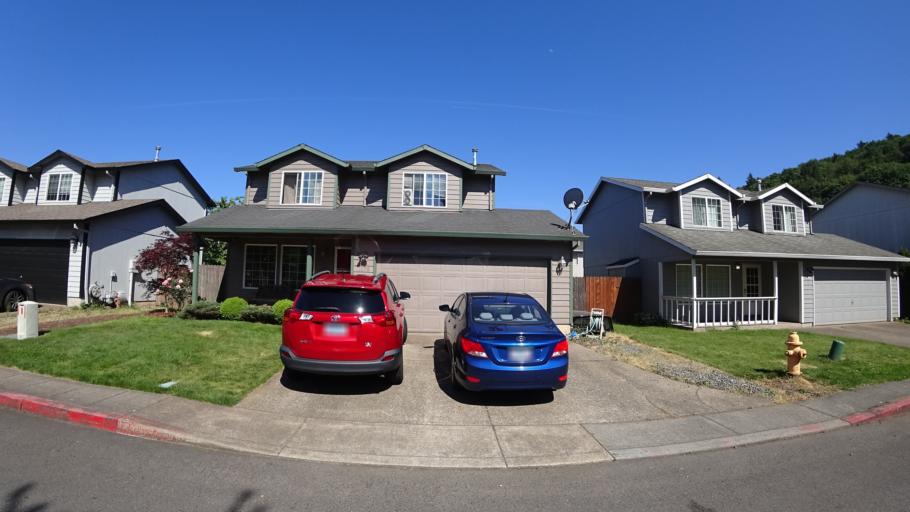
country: US
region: Oregon
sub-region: Multnomah County
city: Gresham
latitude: 45.4877
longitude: -122.4818
